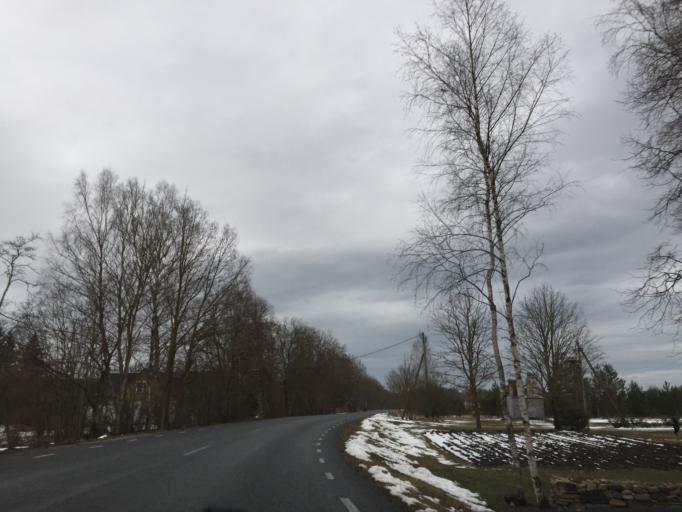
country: EE
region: Saare
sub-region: Orissaare vald
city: Orissaare
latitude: 58.5606
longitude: 22.7735
